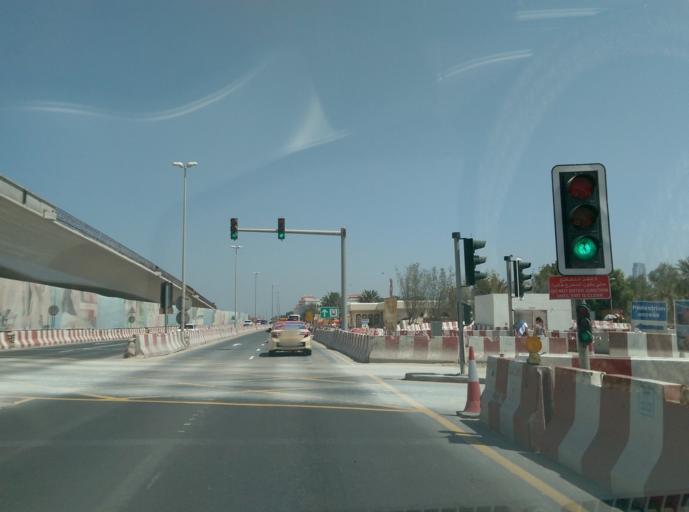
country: AE
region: Dubai
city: Dubai
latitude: 25.1906
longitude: 55.2428
